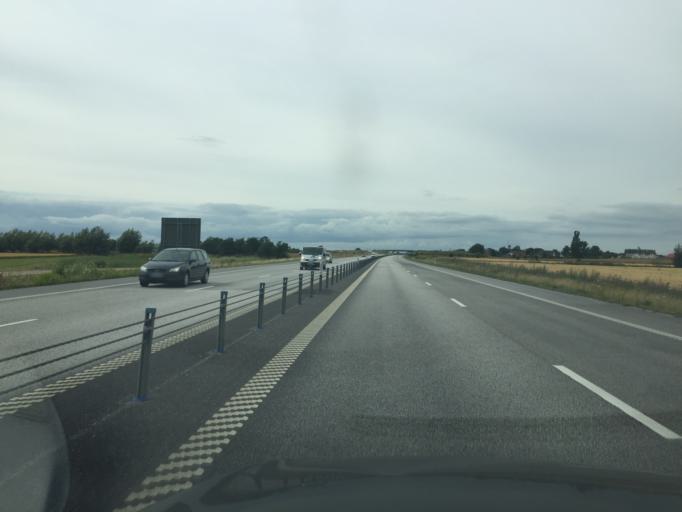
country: SE
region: Skane
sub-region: Vellinge Kommun
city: Vellinge
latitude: 55.4470
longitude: 13.0287
